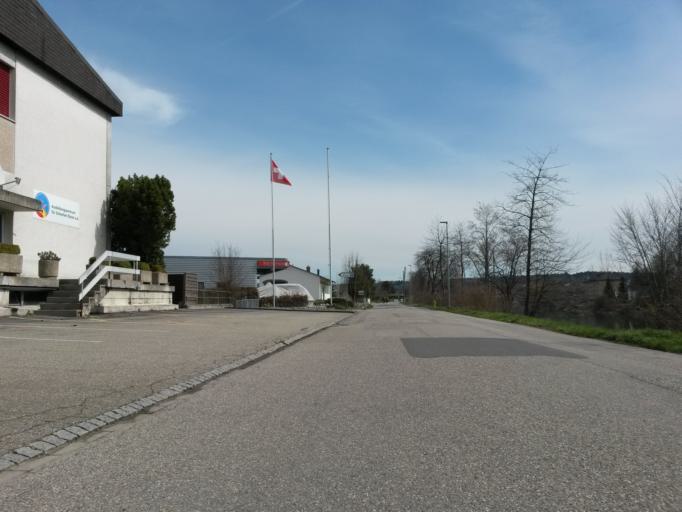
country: CH
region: Bern
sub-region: Biel/Bienne District
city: Meinisberg
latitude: 47.1426
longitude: 7.3603
